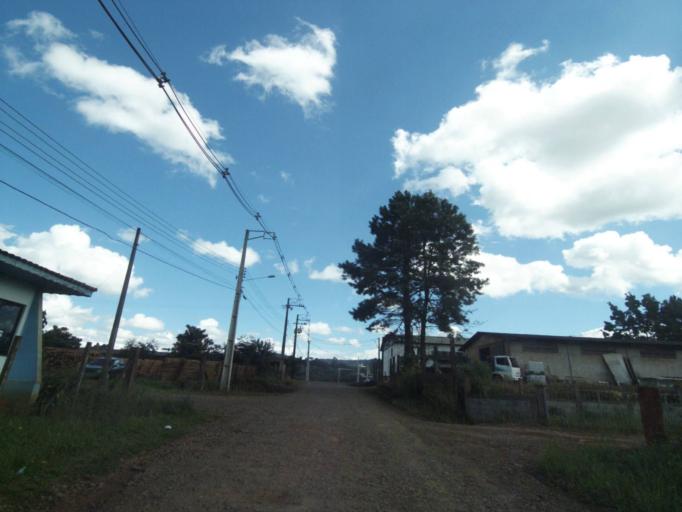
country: BR
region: Parana
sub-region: Uniao Da Vitoria
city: Uniao da Vitoria
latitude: -26.1522
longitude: -51.5385
